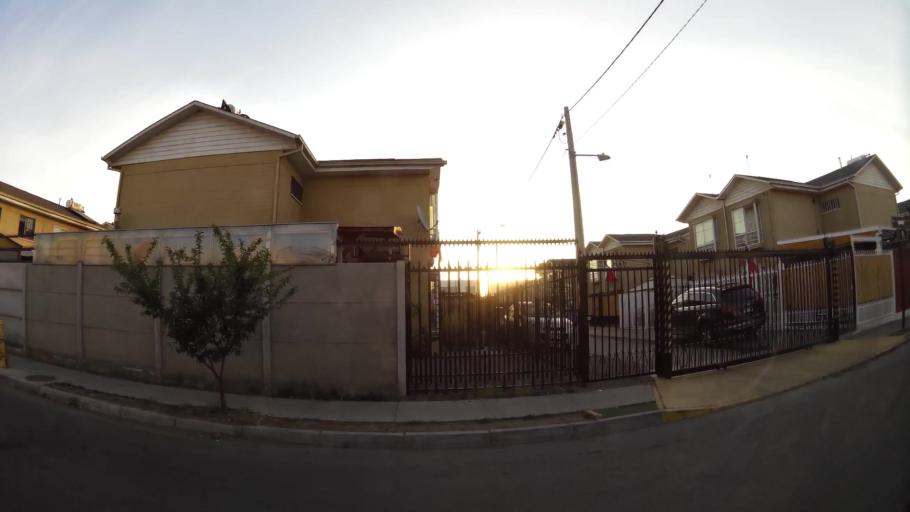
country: CL
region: Santiago Metropolitan
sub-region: Provincia de Cordillera
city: Puente Alto
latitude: -33.6031
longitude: -70.5857
